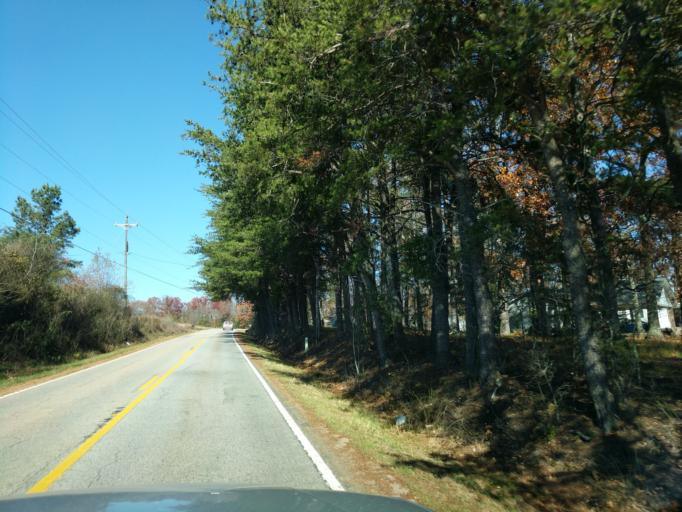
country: US
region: South Carolina
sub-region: Spartanburg County
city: Inman Mills
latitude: 35.0305
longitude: -82.1848
